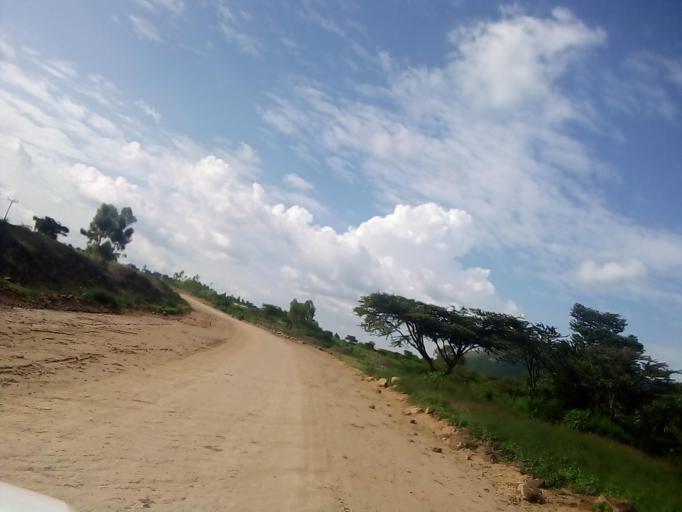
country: ET
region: Southern Nations, Nationalities, and People's Region
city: K'olito
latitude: 7.6235
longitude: 38.0644
